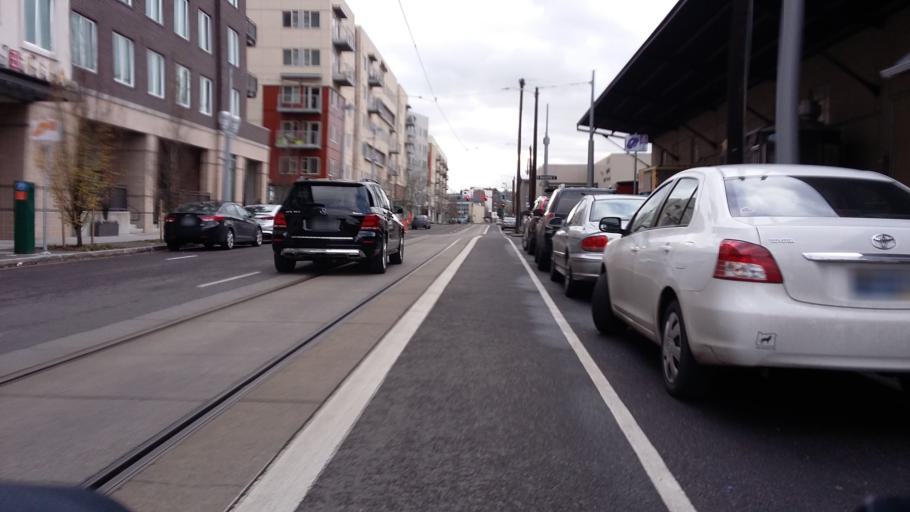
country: US
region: Oregon
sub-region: Multnomah County
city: Portland
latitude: 45.4956
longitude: -122.6720
